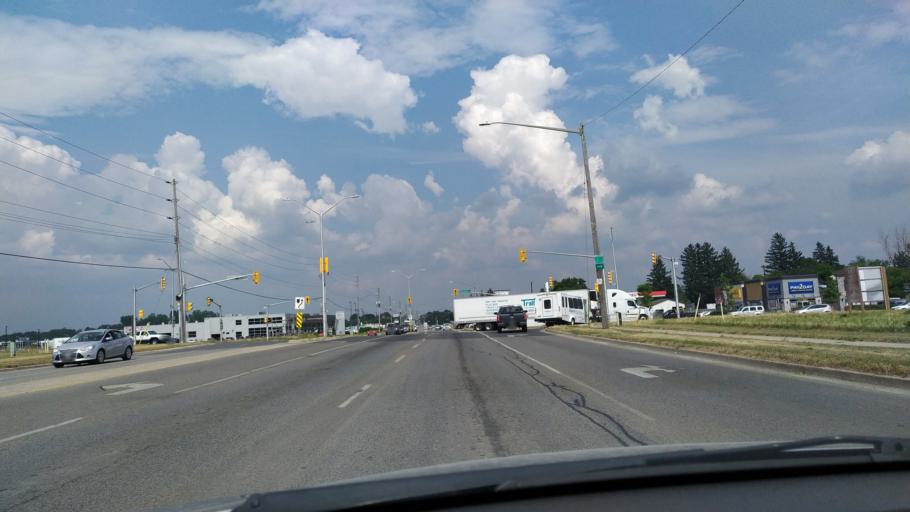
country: CA
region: Ontario
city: London
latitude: 43.0101
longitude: -81.1561
